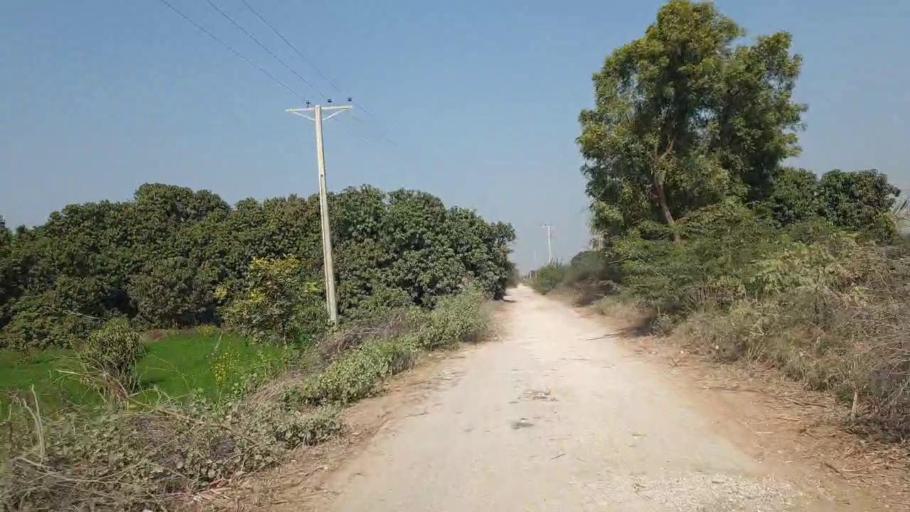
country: PK
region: Sindh
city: Chambar
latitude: 25.4040
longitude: 68.8958
